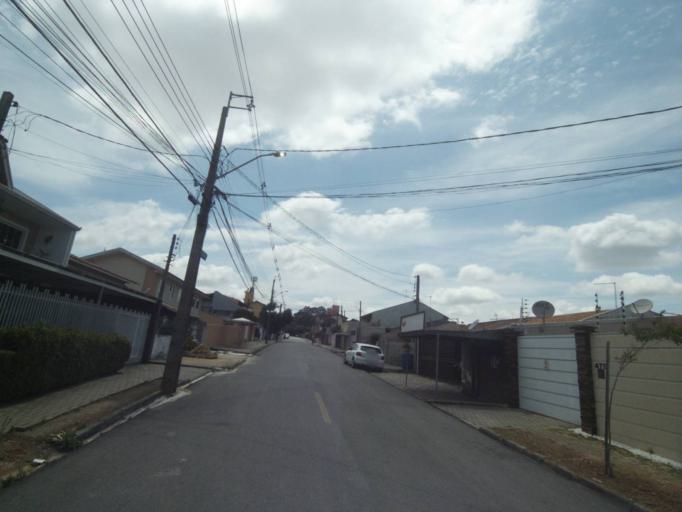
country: BR
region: Parana
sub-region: Curitiba
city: Curitiba
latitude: -25.4524
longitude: -49.3554
